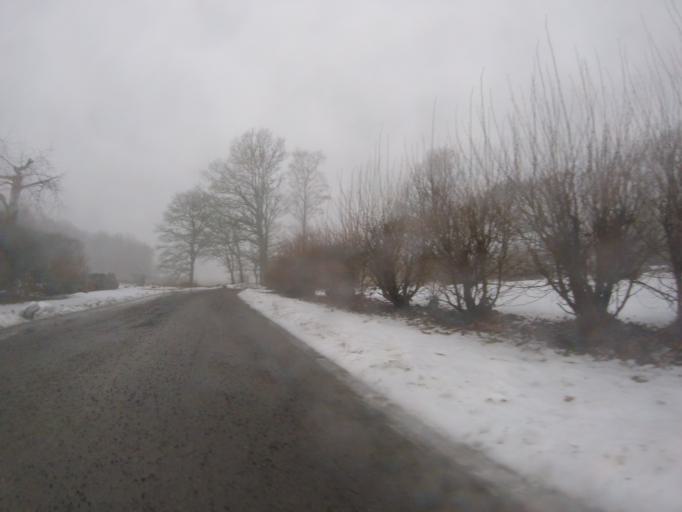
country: SE
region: Halland
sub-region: Varbergs Kommun
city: Varberg
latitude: 57.1939
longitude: 12.2148
